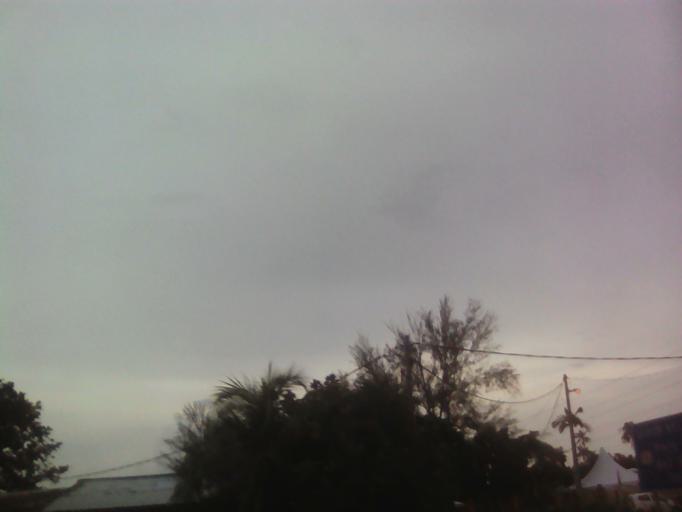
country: MY
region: Penang
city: Perai
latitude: 5.3991
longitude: 100.4097
